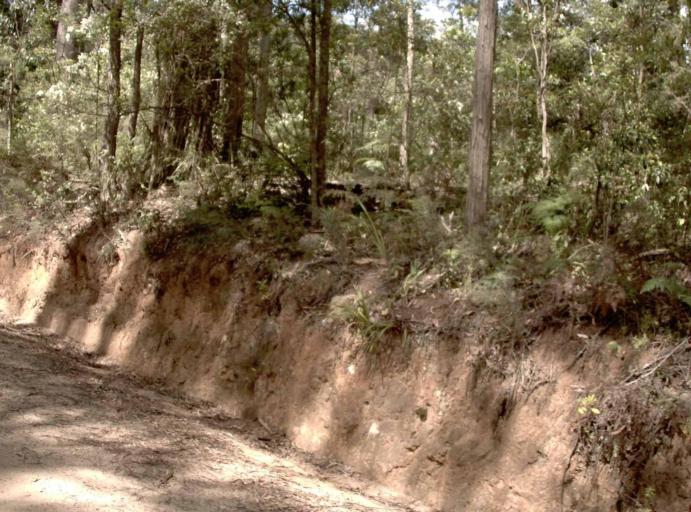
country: AU
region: Victoria
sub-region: East Gippsland
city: Lakes Entrance
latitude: -37.5842
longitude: 148.7262
